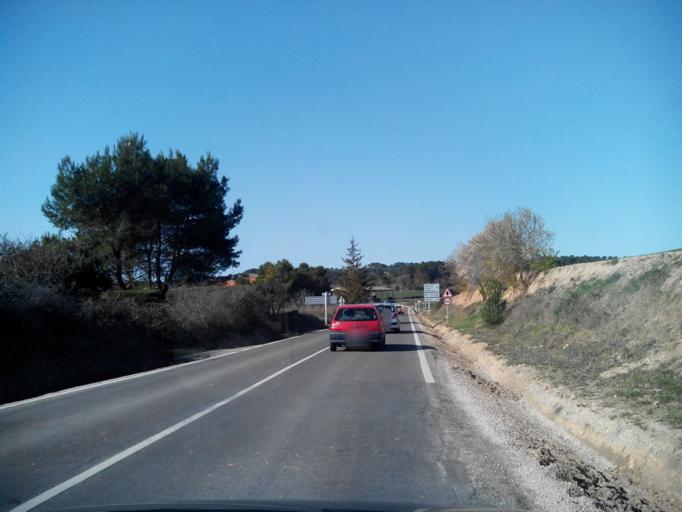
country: ES
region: Catalonia
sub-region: Provincia de Tarragona
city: Conesa
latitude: 41.5051
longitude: 1.3444
